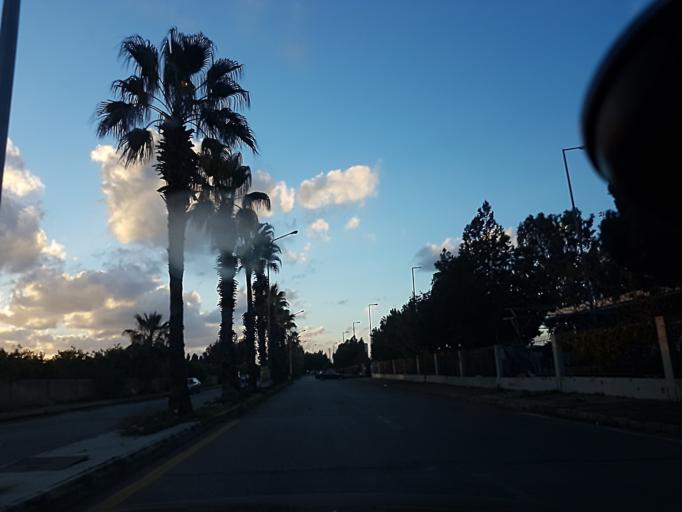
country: LB
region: Liban-Sud
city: Sidon
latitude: 33.5397
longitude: 35.3709
